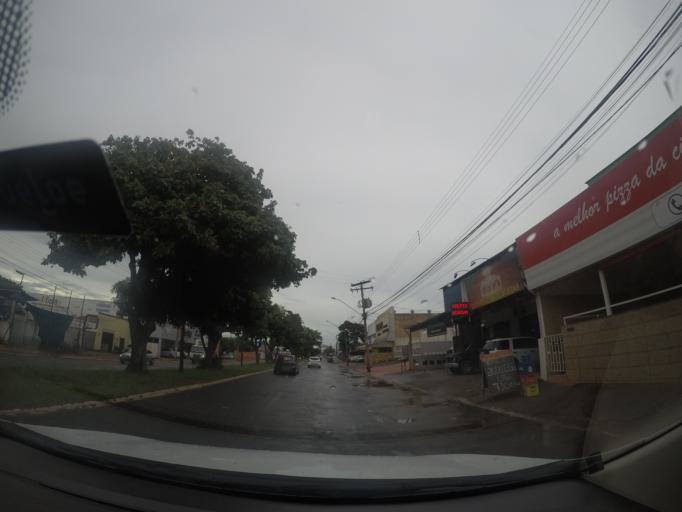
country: BR
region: Goias
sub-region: Goiania
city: Goiania
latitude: -16.6331
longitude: -49.2362
